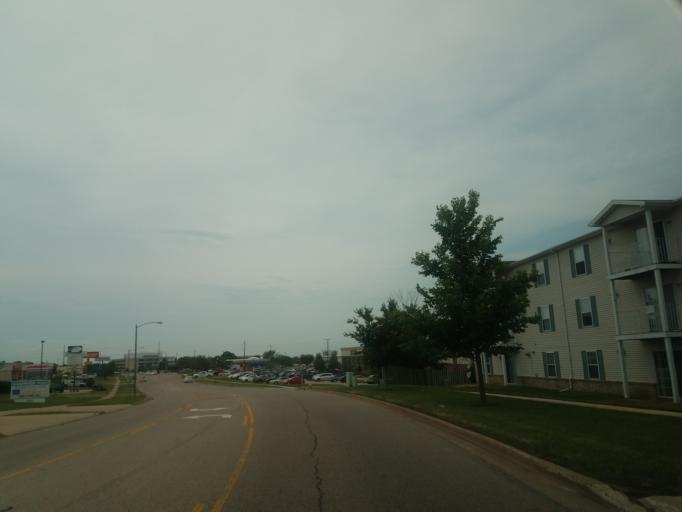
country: US
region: Illinois
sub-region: McLean County
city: Normal
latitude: 40.4966
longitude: -88.9486
